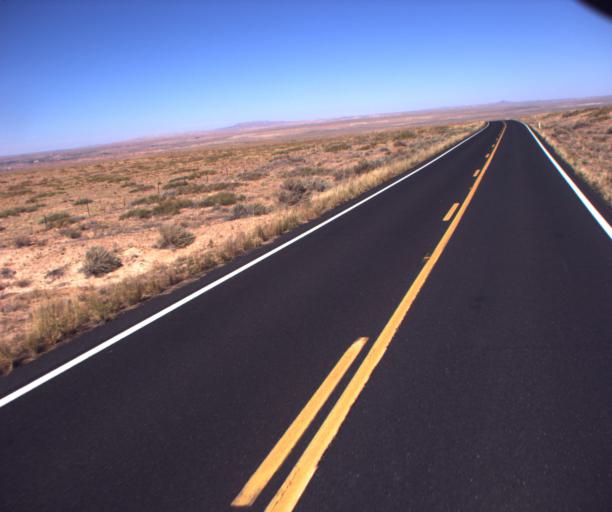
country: US
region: Arizona
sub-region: Coconino County
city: Tuba City
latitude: 36.0459
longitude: -111.1825
